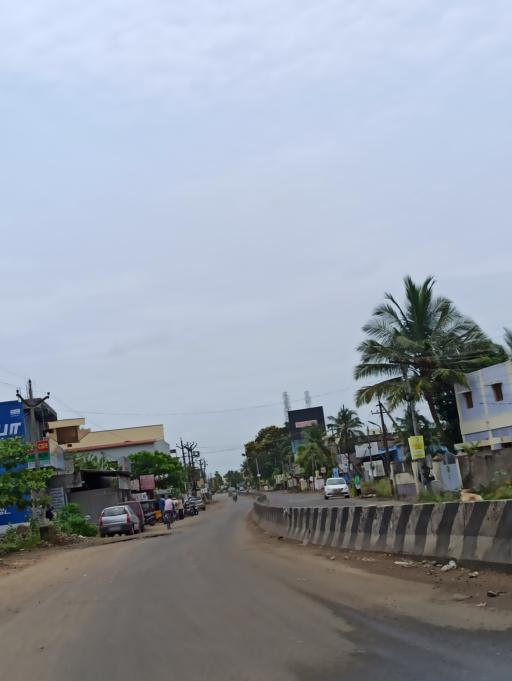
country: IN
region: Tamil Nadu
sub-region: Kancheepuram
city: Vandalur
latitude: 12.9061
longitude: 80.0664
